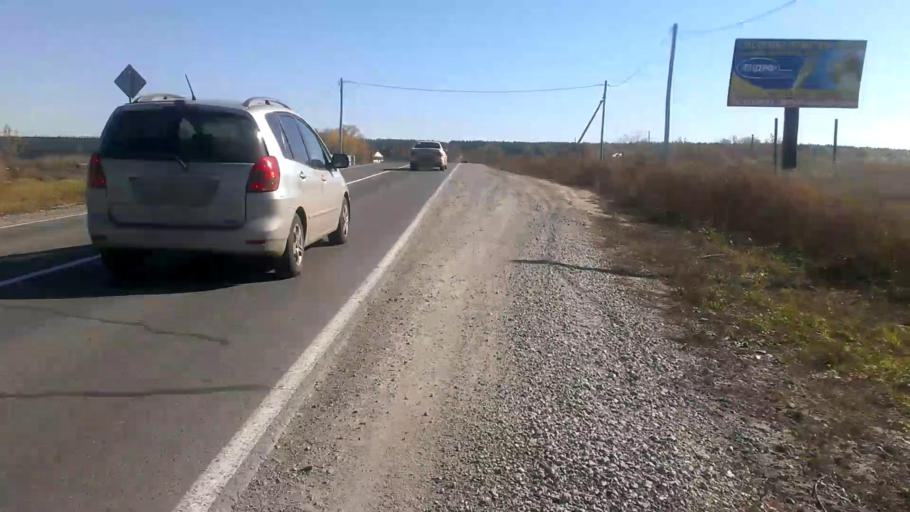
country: RU
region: Altai Krai
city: Sannikovo
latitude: 53.3136
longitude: 83.9622
